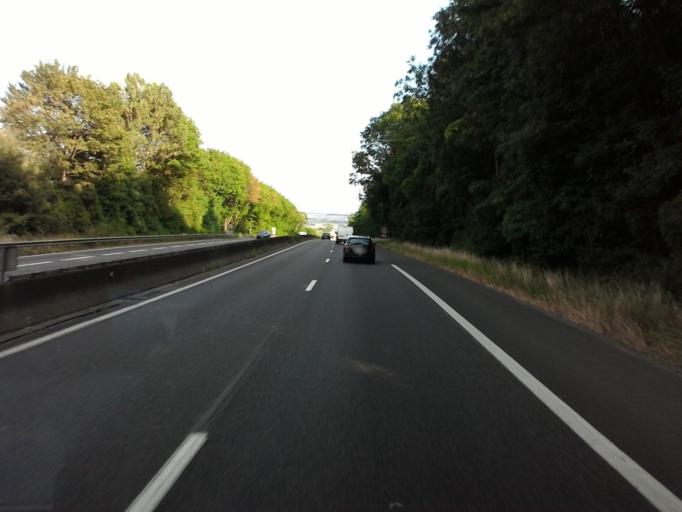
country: FR
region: Lorraine
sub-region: Departement de Meurthe-et-Moselle
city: Ludres
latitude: 48.6360
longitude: 6.1719
